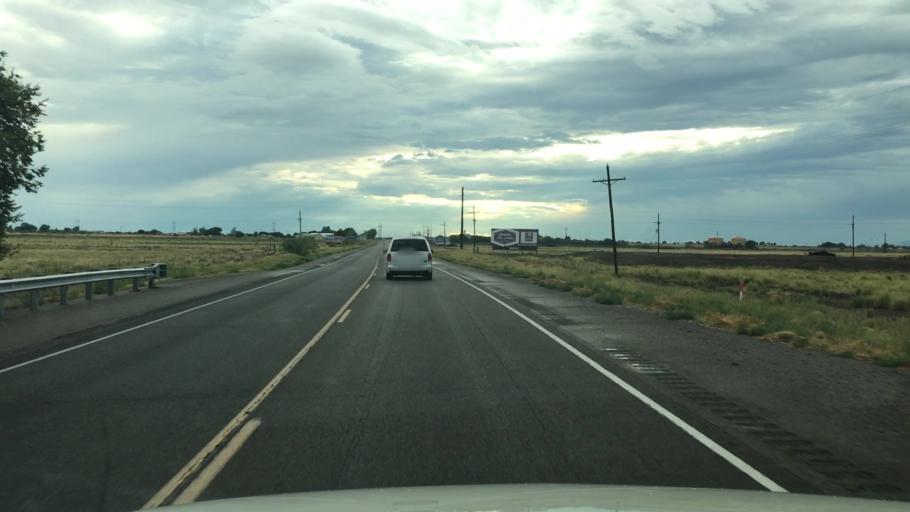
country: US
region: New Mexico
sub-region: Chaves County
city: Roswell
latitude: 33.3972
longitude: -104.4232
